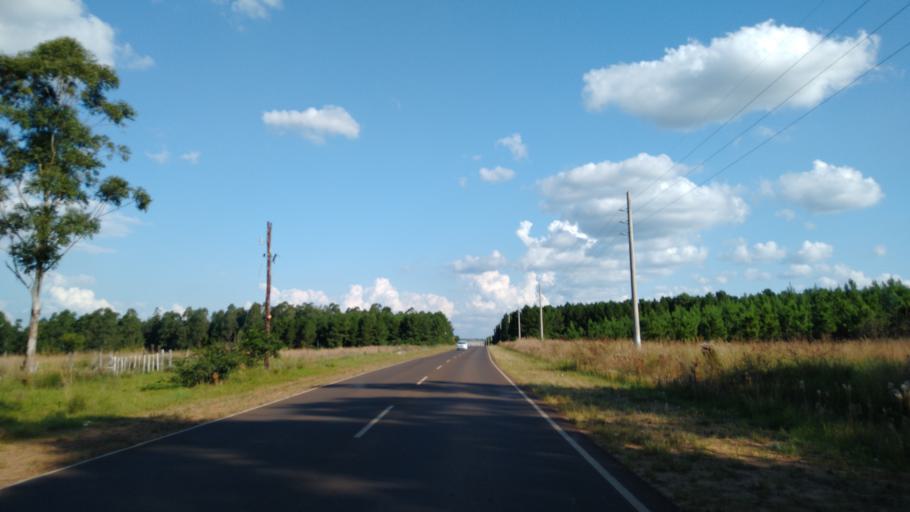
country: PY
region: Itapua
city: San Juan del Parana
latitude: -27.3796
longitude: -55.9918
